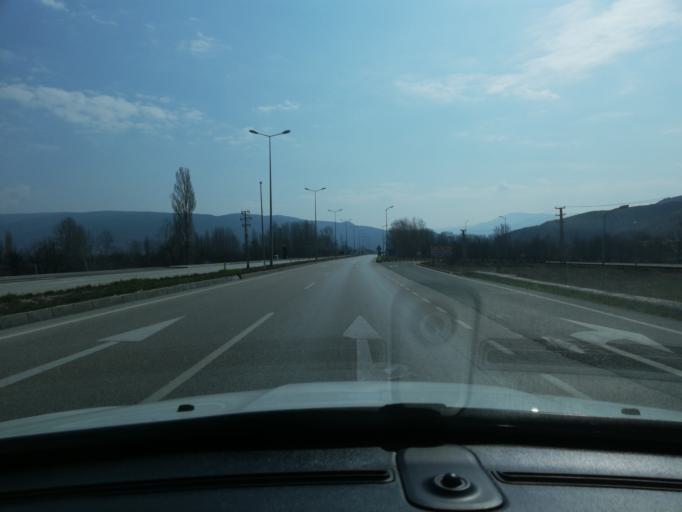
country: TR
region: Cankiri
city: Ilgaz
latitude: 40.9082
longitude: 33.6348
